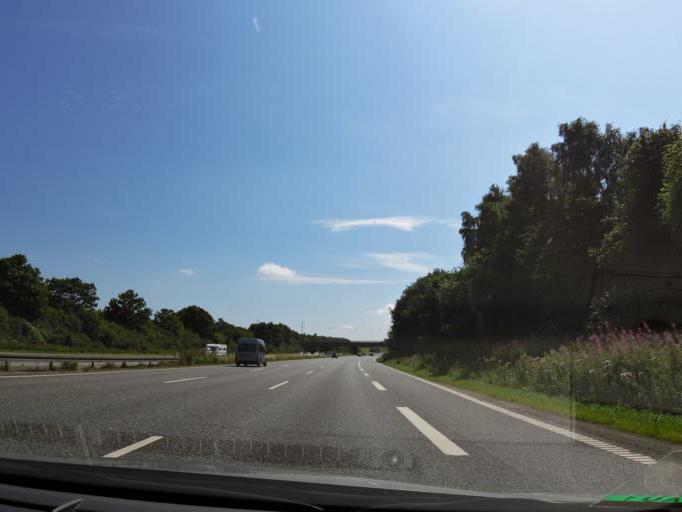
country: DK
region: South Denmark
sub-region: Fredericia Kommune
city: Snoghoj
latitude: 55.5345
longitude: 9.7118
